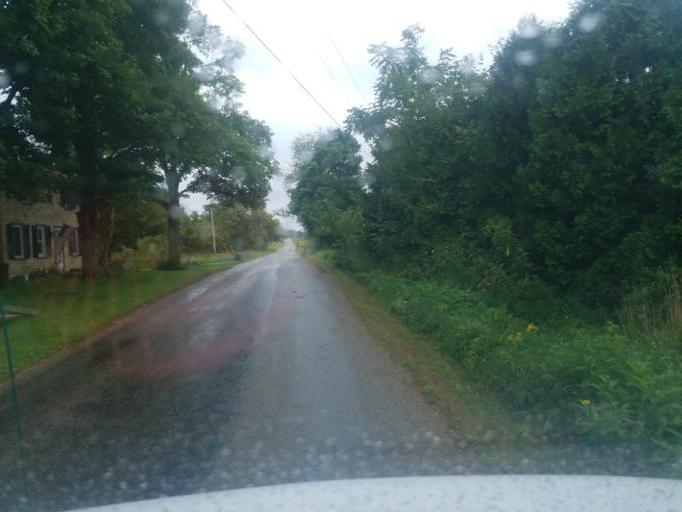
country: US
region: Ohio
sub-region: Wayne County
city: West Salem
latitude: 40.9197
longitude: -82.1186
